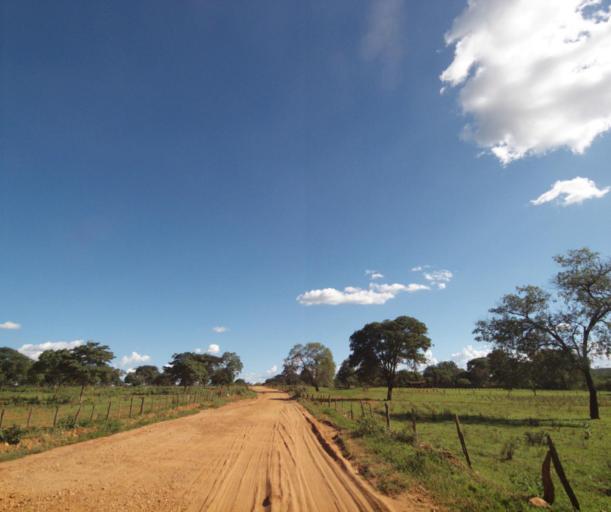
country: BR
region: Bahia
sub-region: Carinhanha
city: Carinhanha
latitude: -14.2068
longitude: -44.5415
